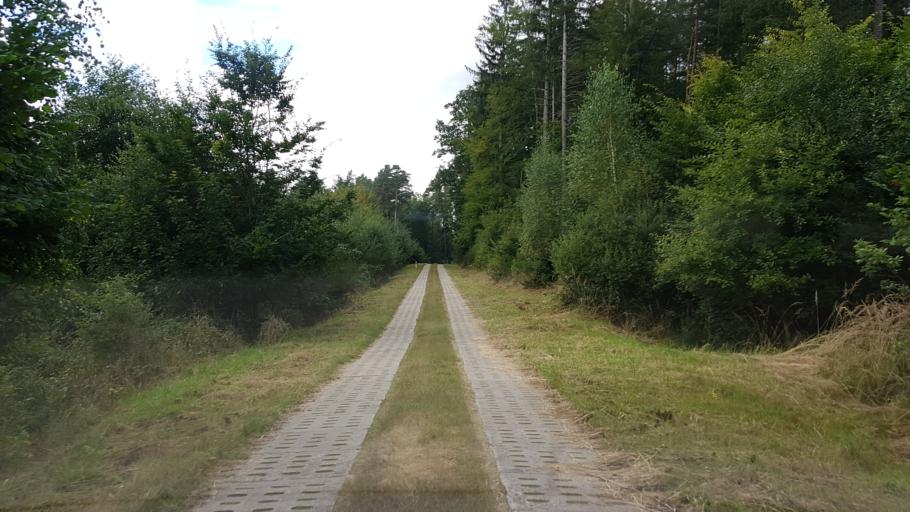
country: PL
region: West Pomeranian Voivodeship
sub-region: Powiat szczecinecki
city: Grzmiaca
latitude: 53.9655
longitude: 16.3935
